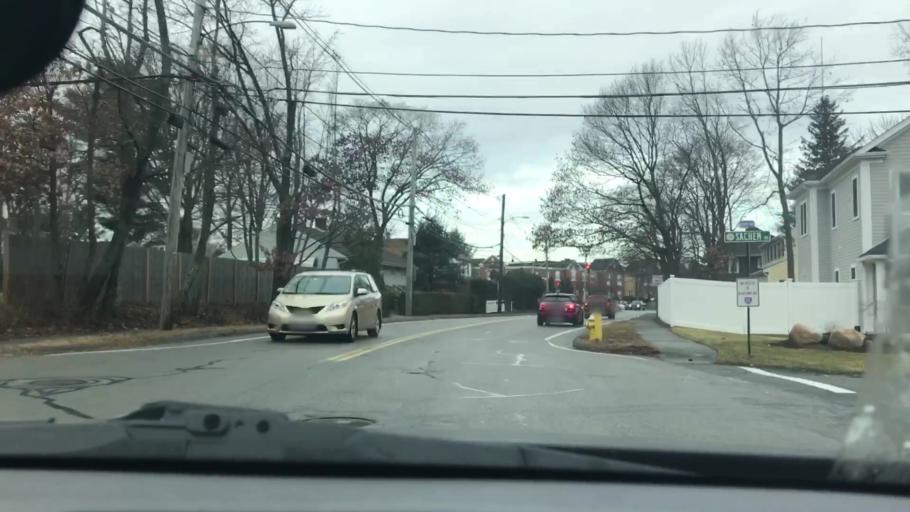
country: US
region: Massachusetts
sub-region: Norfolk County
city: Needham
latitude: 42.2996
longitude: -71.2281
